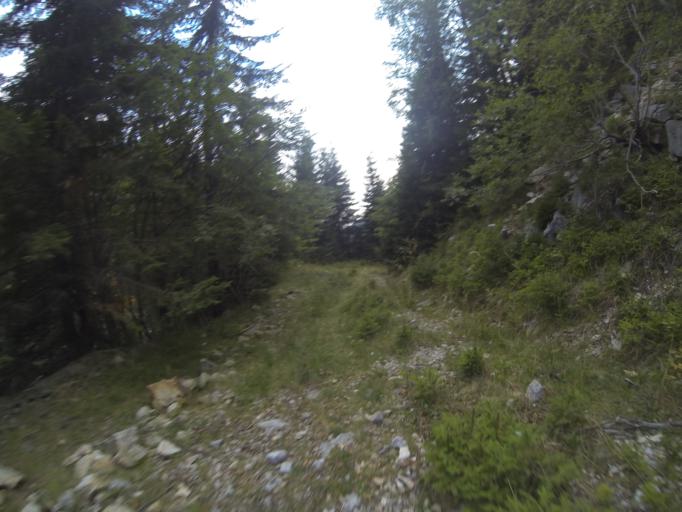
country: RO
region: Gorj
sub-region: Comuna Polovragi
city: Polovragi
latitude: 45.2774
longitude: 23.8331
